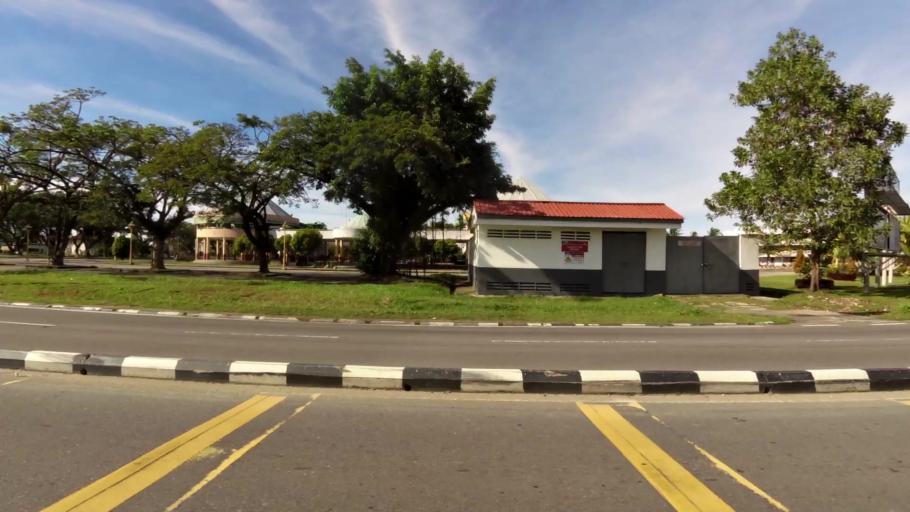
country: BN
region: Belait
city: Kuala Belait
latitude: 4.5768
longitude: 114.1985
